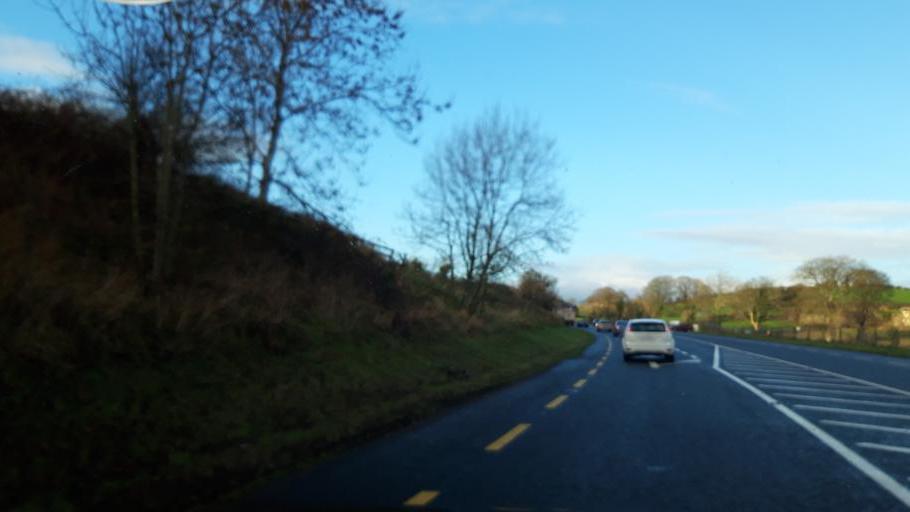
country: IE
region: Ulster
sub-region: County Monaghan
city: Castleblayney
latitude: 54.0613
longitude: -6.6970
